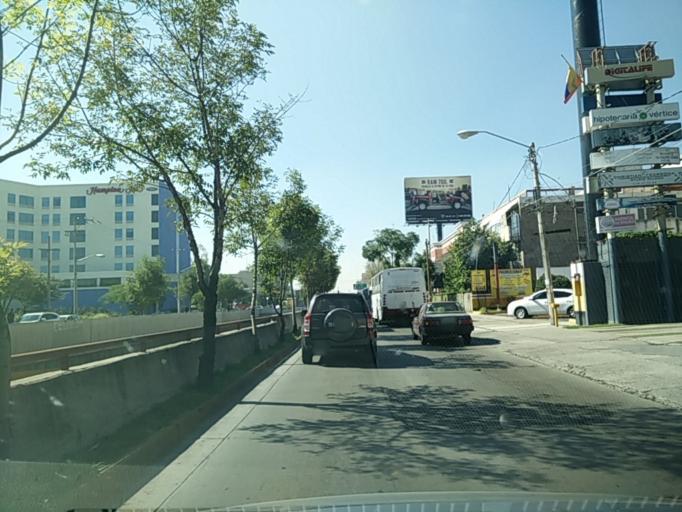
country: MX
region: Jalisco
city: Guadalajara
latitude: 20.6606
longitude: -103.3966
